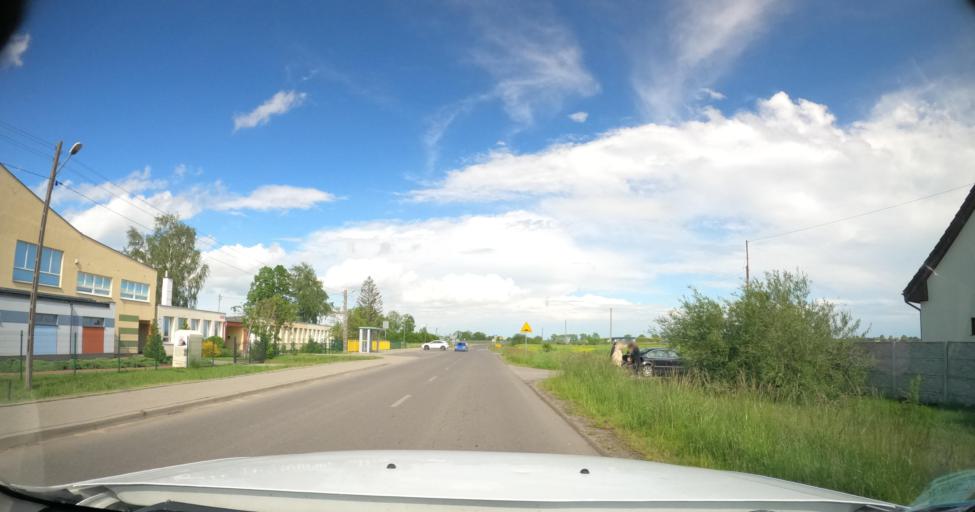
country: PL
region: Pomeranian Voivodeship
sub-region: Powiat nowodworski
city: Nowy Dwor Gdanski
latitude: 54.1892
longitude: 19.1591
